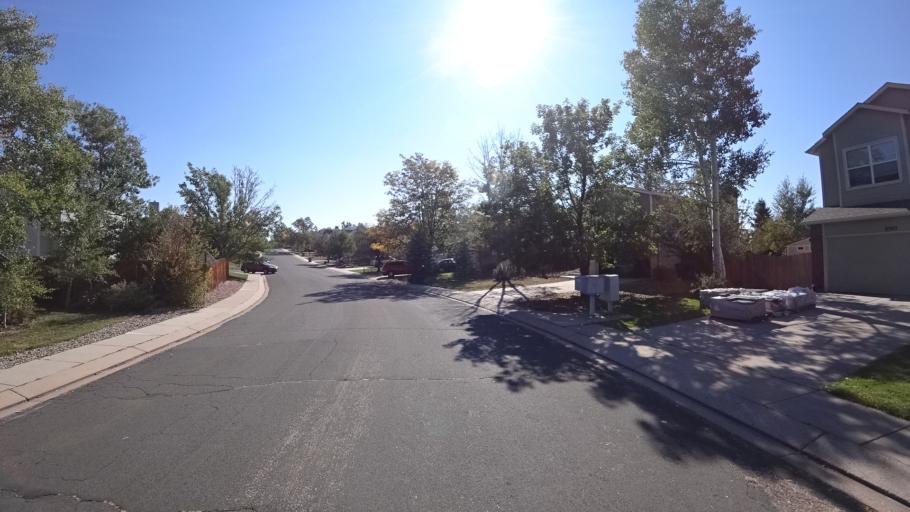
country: US
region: Colorado
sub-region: El Paso County
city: Cimarron Hills
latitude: 38.8756
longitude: -104.7056
